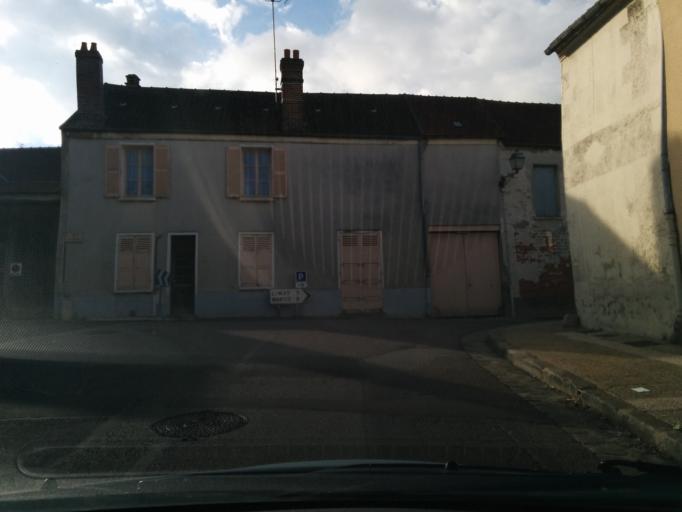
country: FR
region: Ile-de-France
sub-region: Departement des Yvelines
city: Follainville-Dennemont
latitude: 49.0403
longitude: 1.6893
